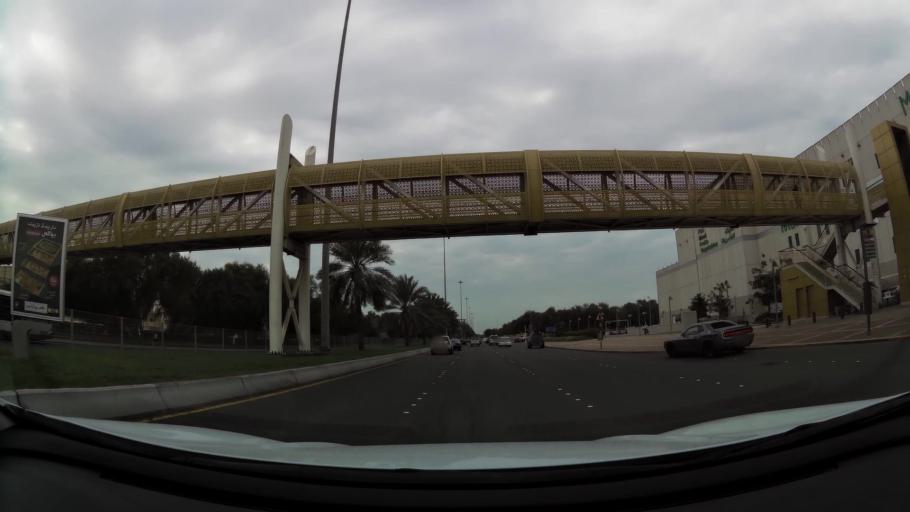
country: AE
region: Abu Dhabi
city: Abu Dhabi
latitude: 24.4336
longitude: 54.4119
